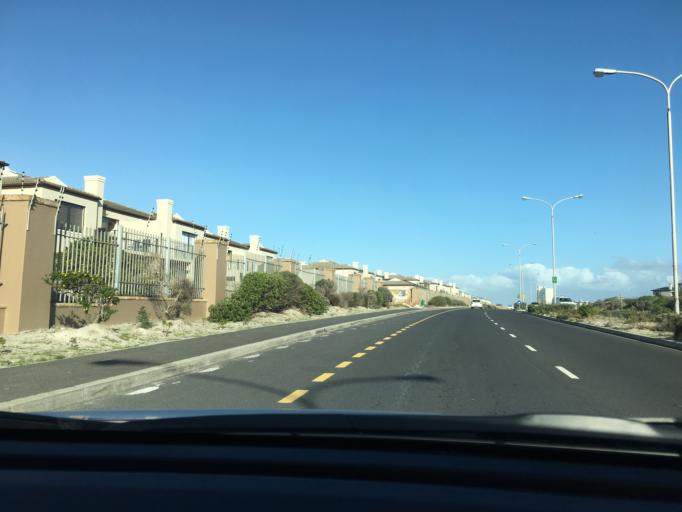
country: ZA
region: Western Cape
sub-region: City of Cape Town
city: Sunset Beach
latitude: -33.7939
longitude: 18.4614
